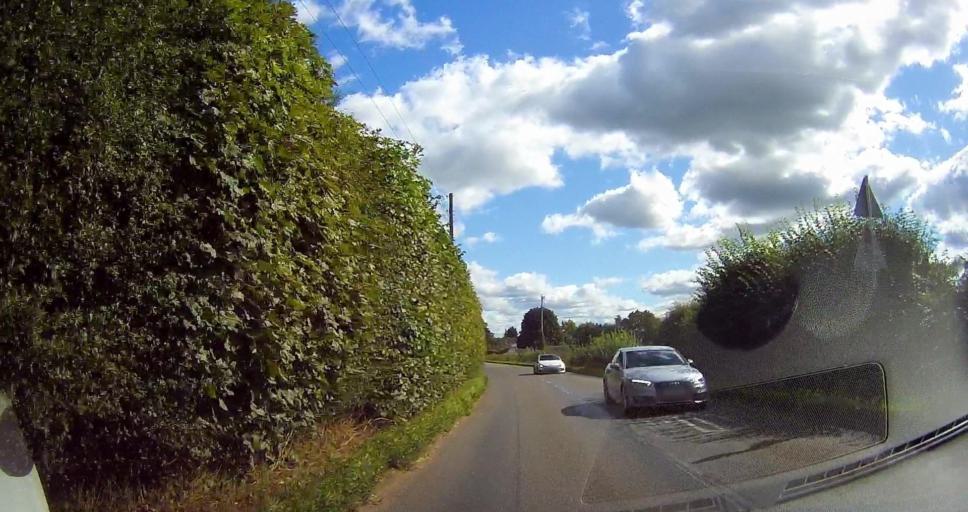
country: GB
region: England
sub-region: Staffordshire
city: Standon
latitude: 52.9566
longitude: -2.3736
